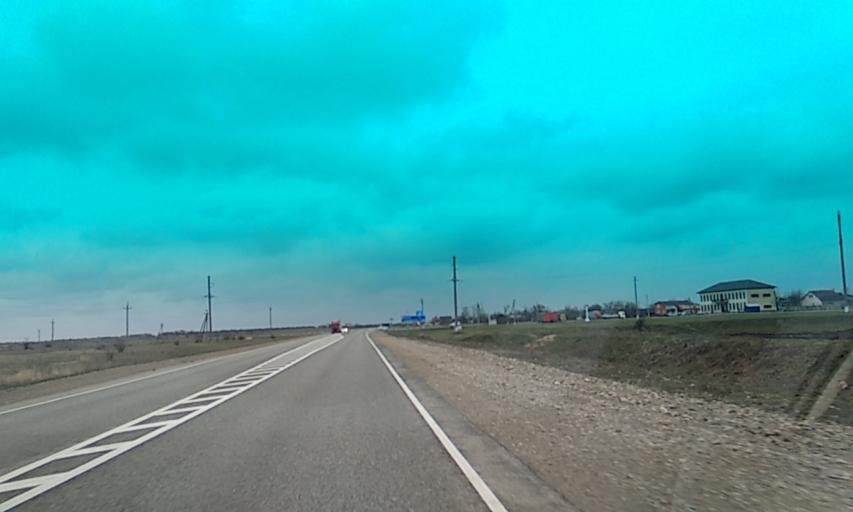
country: RU
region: Krasnodarskiy
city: Velikovechnoye
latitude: 44.9305
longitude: 39.7791
